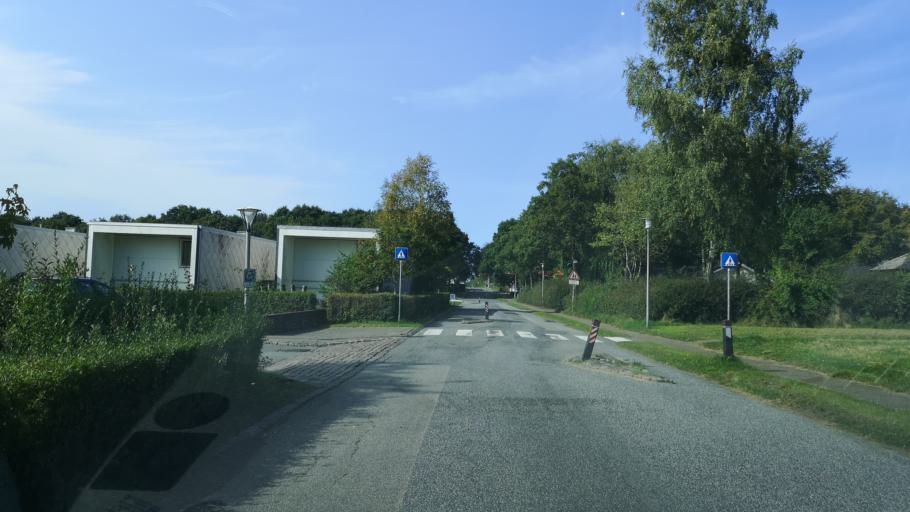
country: DK
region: Central Jutland
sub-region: Herning Kommune
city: Herning
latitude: 56.1673
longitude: 8.9746
